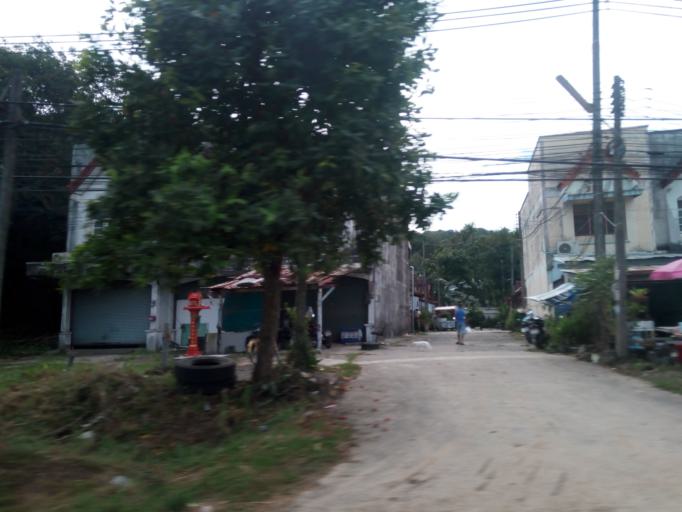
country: TH
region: Phuket
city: Mueang Phuket
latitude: 7.8380
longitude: 98.3930
